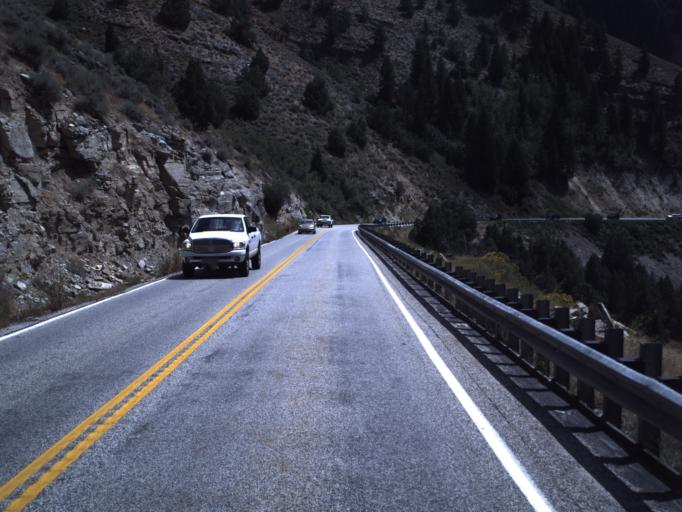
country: US
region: Utah
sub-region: Cache County
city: North Logan
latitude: 41.8283
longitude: -111.6025
